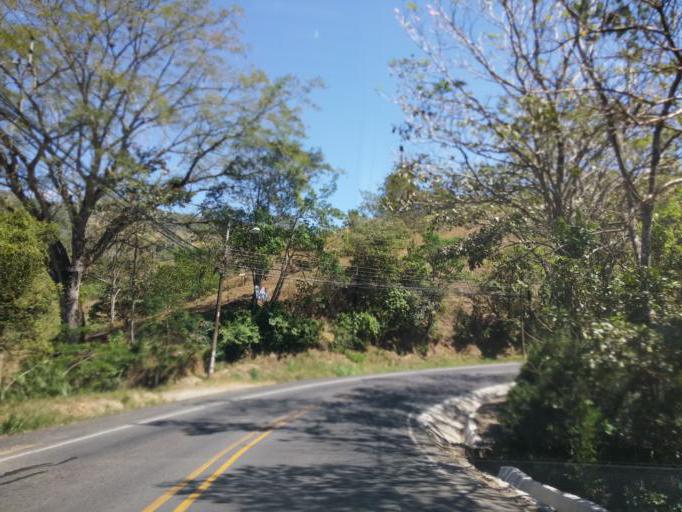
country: CR
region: Heredia
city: Colon
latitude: 9.8966
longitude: -84.2345
